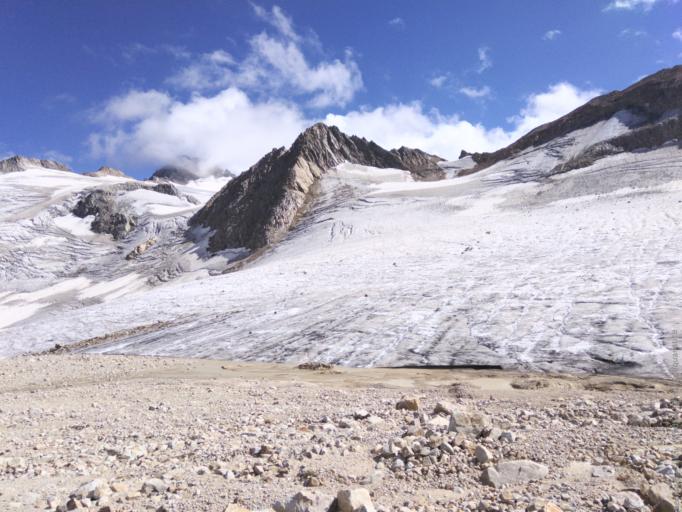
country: RU
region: Kabardino-Balkariya
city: Terskol
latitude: 43.2600
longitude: 42.4264
